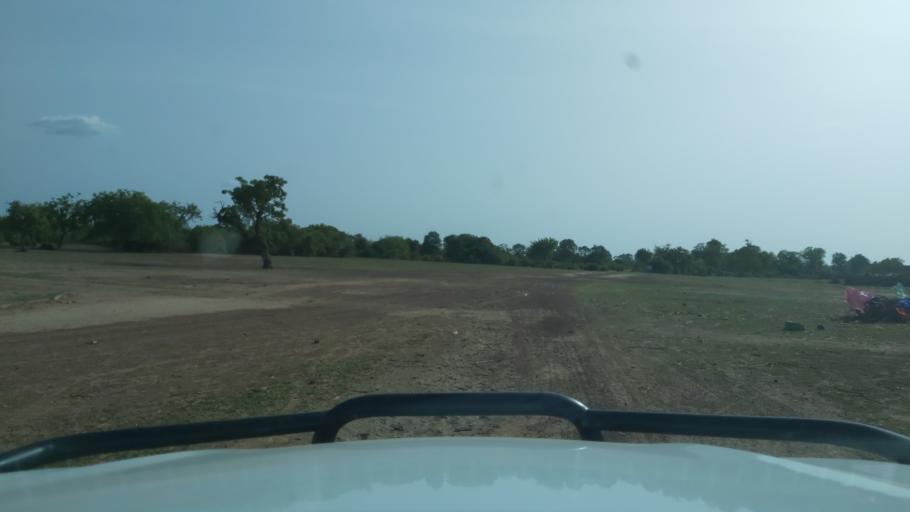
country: ML
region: Koulikoro
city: Koulikoro
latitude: 13.1646
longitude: -7.7947
